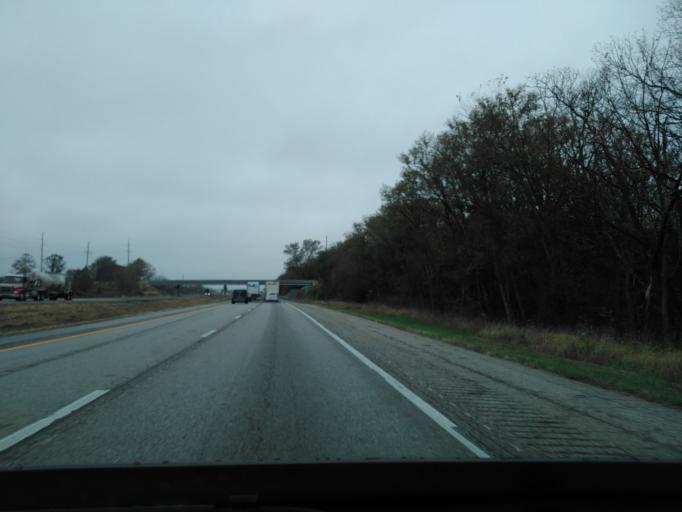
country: US
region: Illinois
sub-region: Madison County
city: Highland
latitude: 38.8034
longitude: -89.5963
